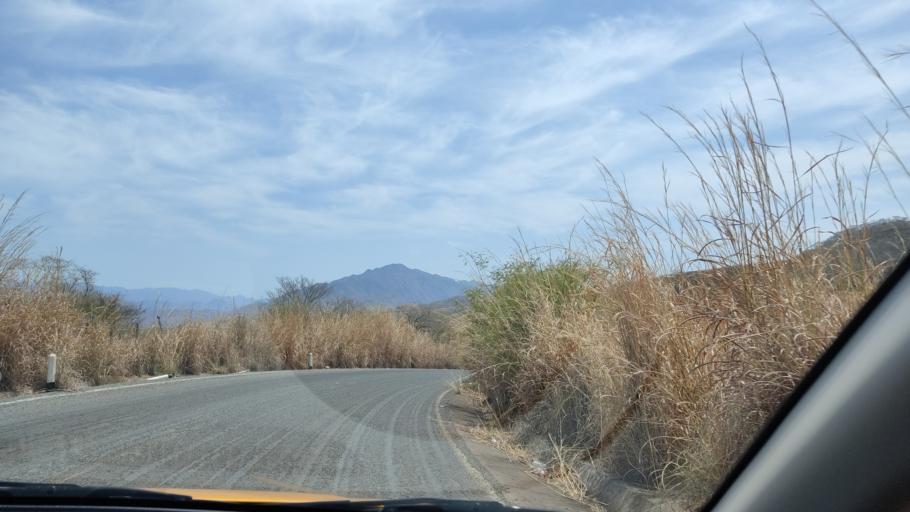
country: MX
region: Nayarit
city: Santa Maria del Oro
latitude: 21.5082
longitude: -104.6064
